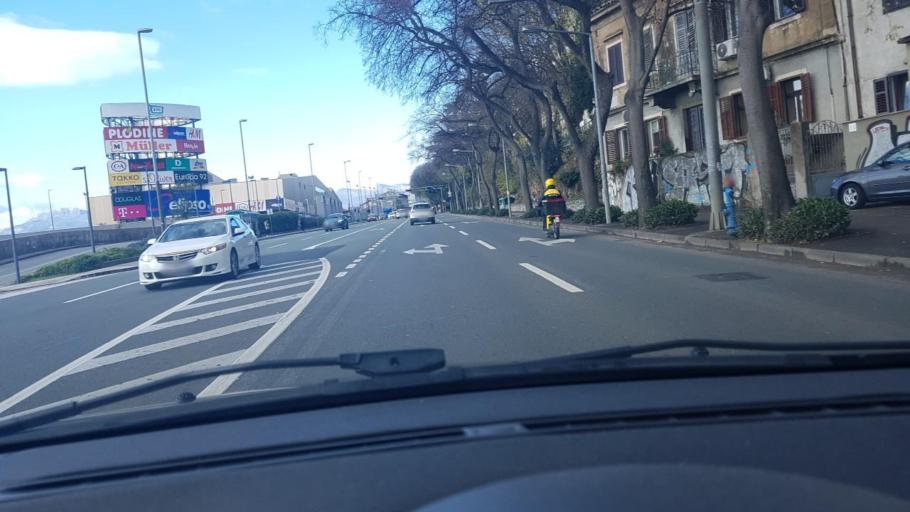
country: HR
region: Primorsko-Goranska
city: Rijeka
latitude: 45.3381
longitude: 14.4110
